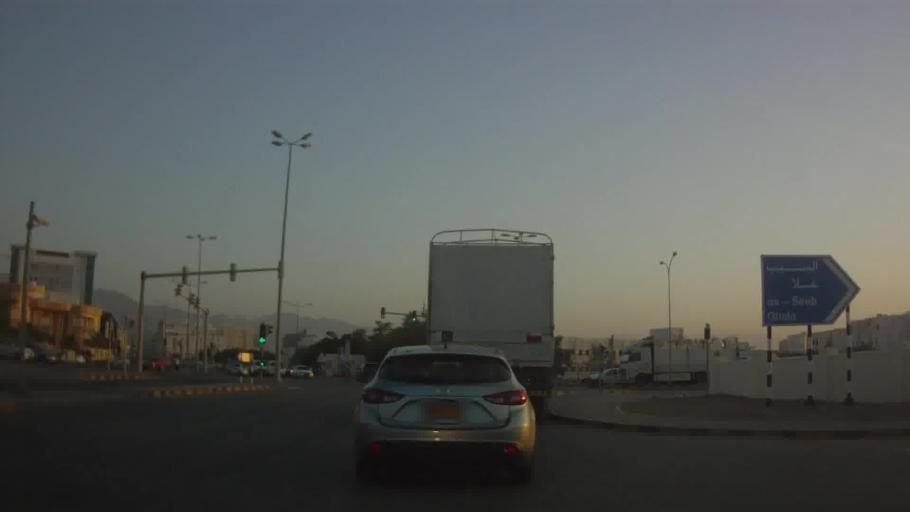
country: OM
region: Muhafazat Masqat
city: Bawshar
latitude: 23.5975
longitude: 58.4019
